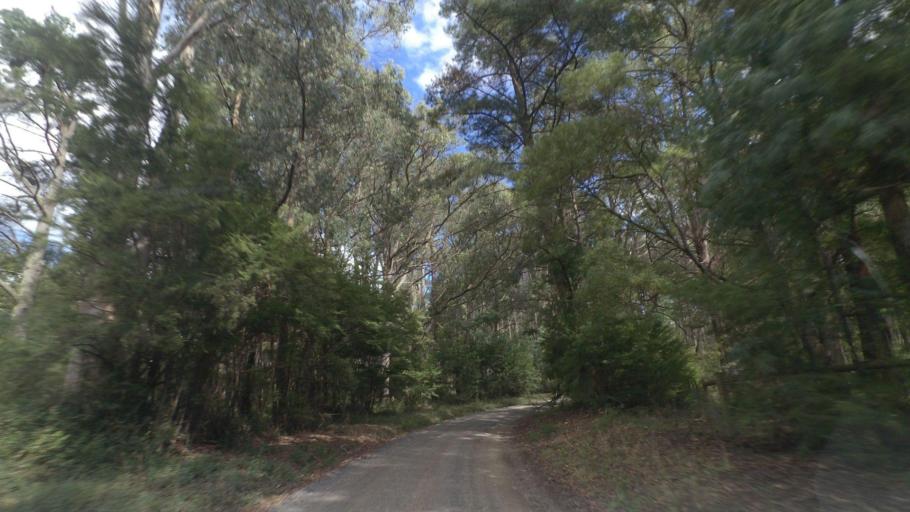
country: AU
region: Victoria
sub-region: Cardinia
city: Gembrook
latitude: -37.9035
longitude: 145.6165
